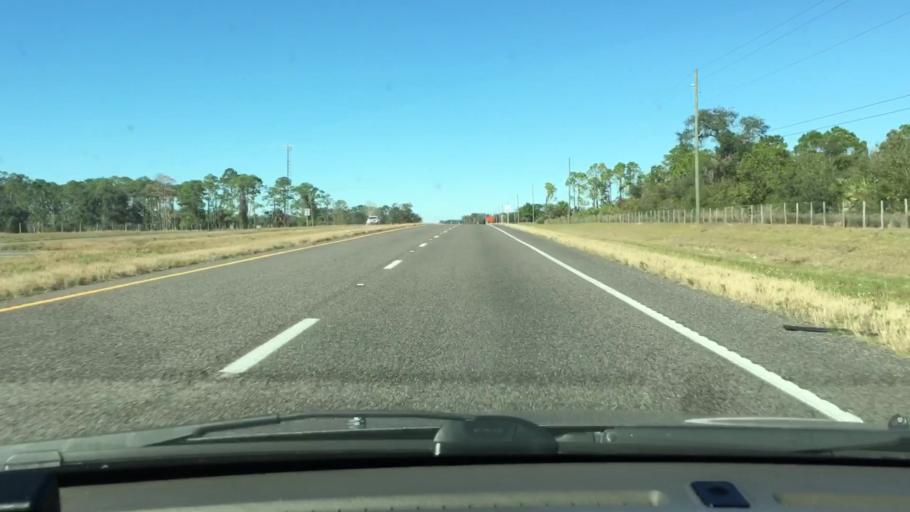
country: US
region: Florida
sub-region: Brevard County
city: June Park
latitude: 28.0980
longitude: -80.8924
